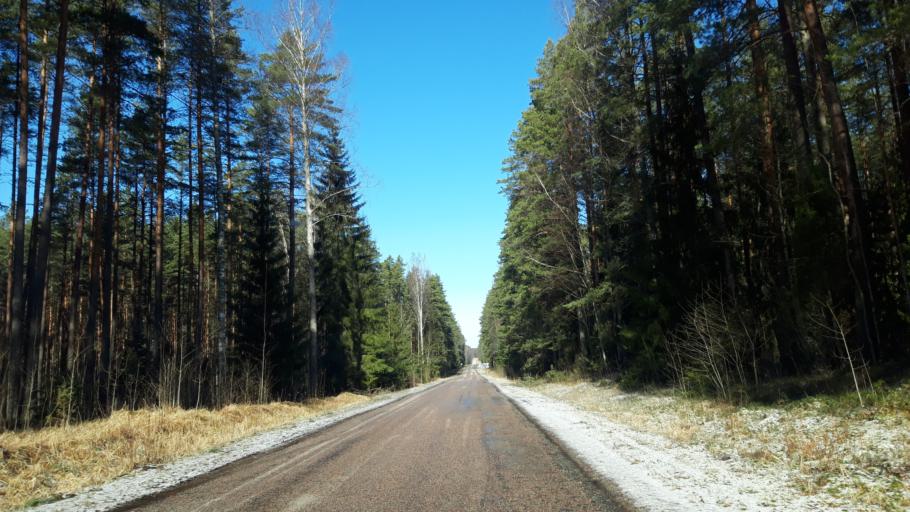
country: LV
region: Strenci
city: Strenci
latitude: 57.5967
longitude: 25.7185
